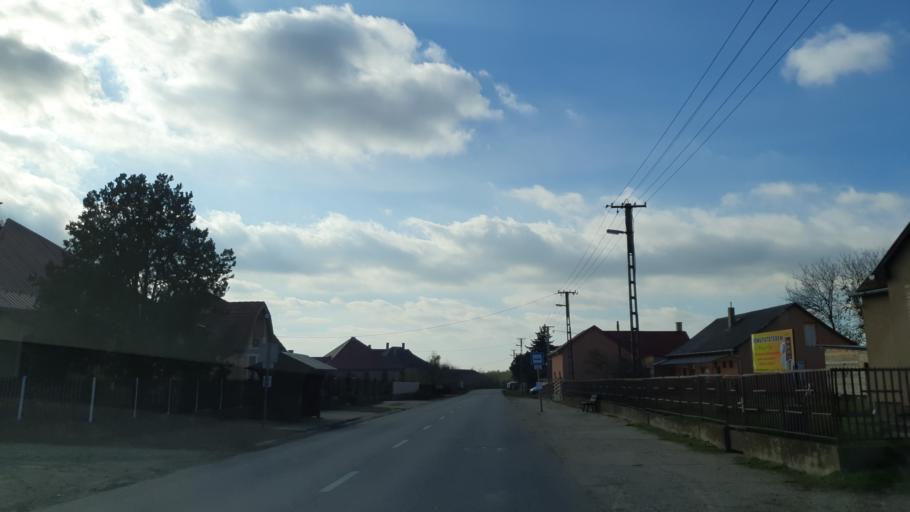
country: HU
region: Szabolcs-Szatmar-Bereg
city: Nyirkarasz
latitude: 48.0946
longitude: 22.0978
